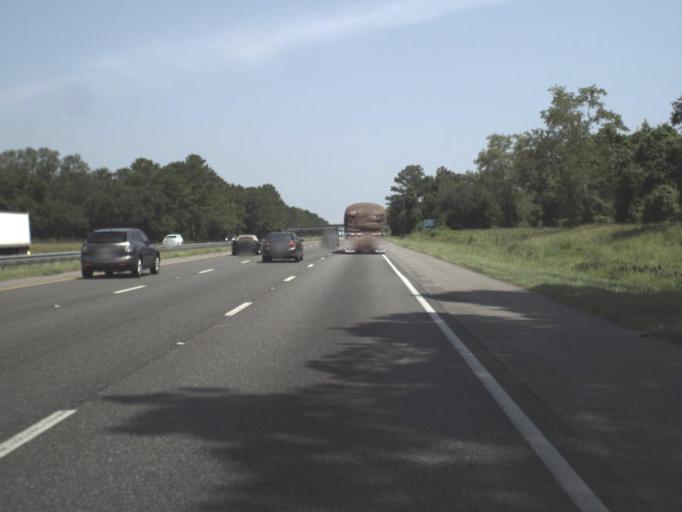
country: US
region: Florida
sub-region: Hamilton County
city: Jasper
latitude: 30.4045
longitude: -82.8880
